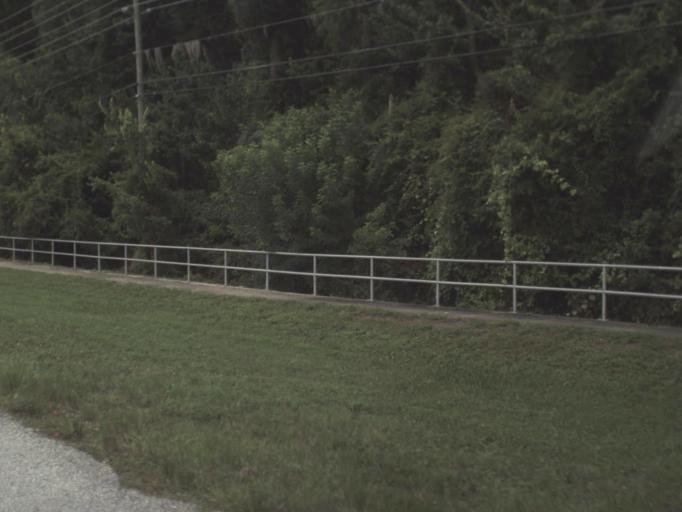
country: US
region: Florida
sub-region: Pasco County
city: Trinity
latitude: 28.1620
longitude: -82.6975
